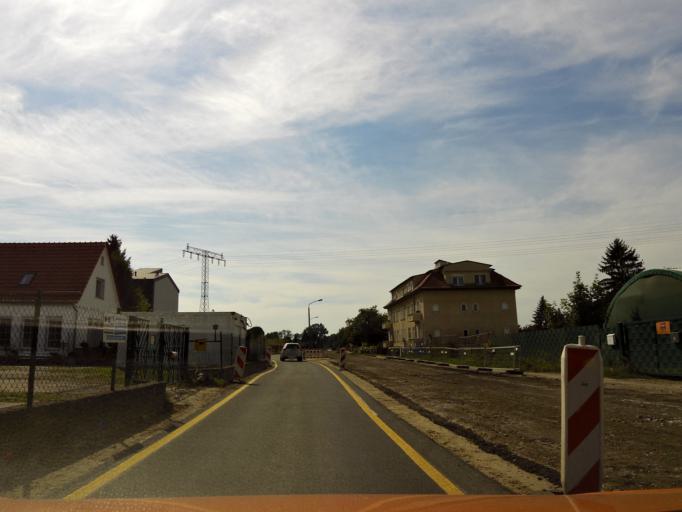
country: DE
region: Brandenburg
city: Teltow
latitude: 52.3934
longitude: 13.2664
